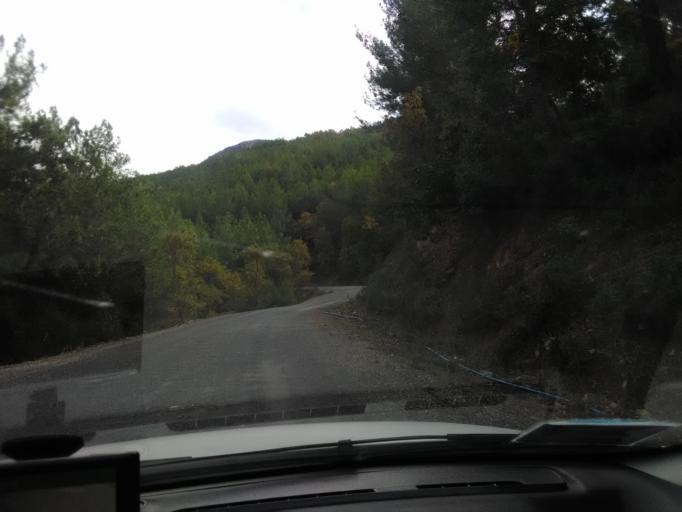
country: TR
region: Antalya
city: Gazipasa
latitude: 36.2472
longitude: 32.4386
